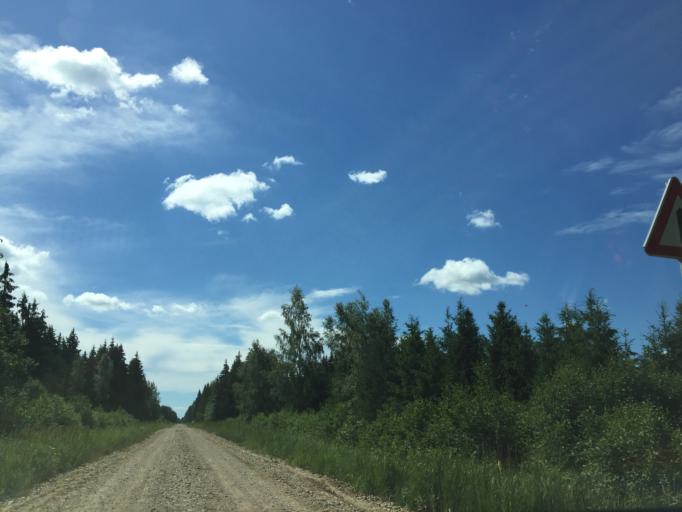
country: LV
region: Ventspils Rajons
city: Piltene
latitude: 57.2742
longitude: 21.8331
